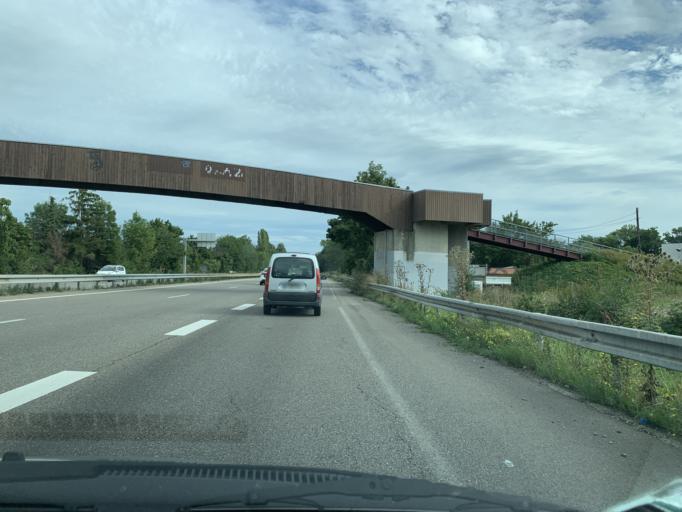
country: FR
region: Alsace
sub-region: Departement du Haut-Rhin
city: Lutterbach
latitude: 47.7571
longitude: 7.2676
